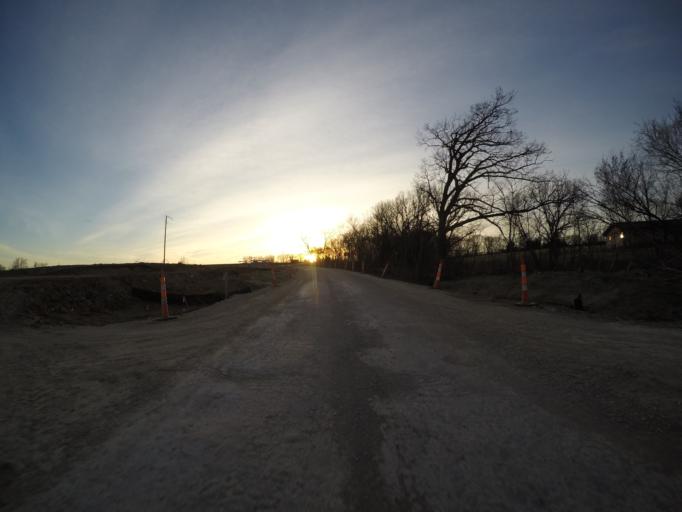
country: US
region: Kansas
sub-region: Clay County
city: Clay Center
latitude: 39.4375
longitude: -96.8962
